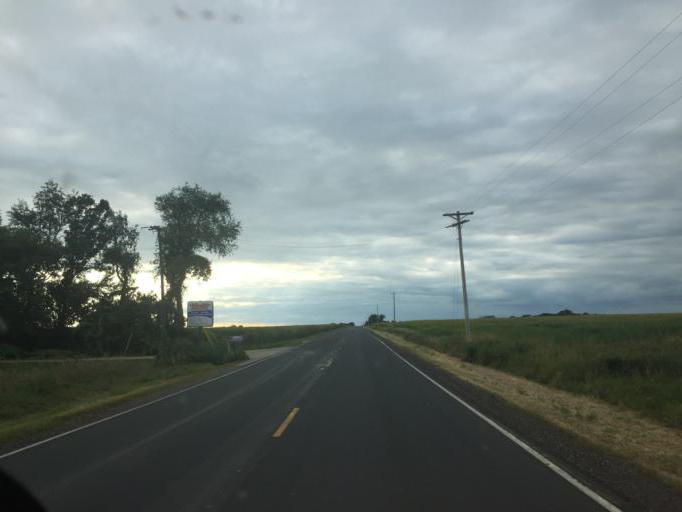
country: US
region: Minnesota
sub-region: Olmsted County
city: Rochester
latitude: 43.9639
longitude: -92.4976
